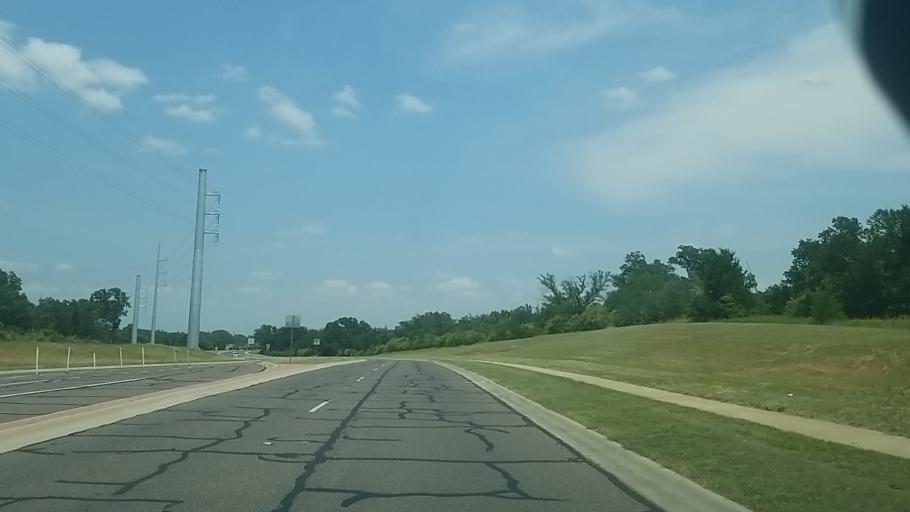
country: US
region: Texas
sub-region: Denton County
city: Denton
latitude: 33.2035
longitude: -97.0964
